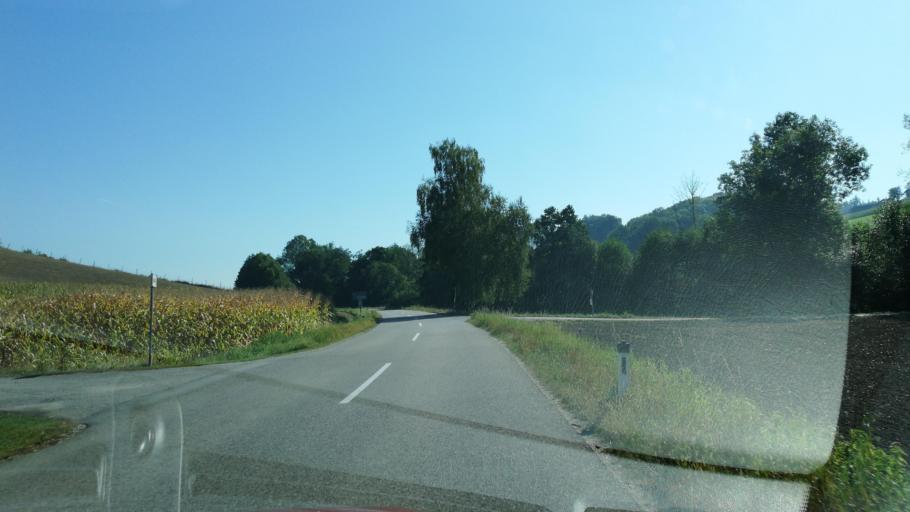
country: AT
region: Upper Austria
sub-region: Politischer Bezirk Grieskirchen
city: Grieskirchen
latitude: 48.1999
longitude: 13.8568
